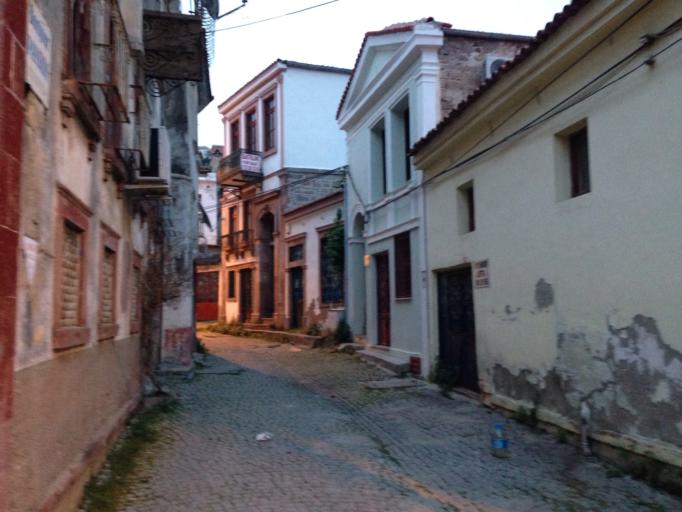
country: TR
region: Balikesir
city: Ayvalik
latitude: 39.3206
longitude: 26.6938
